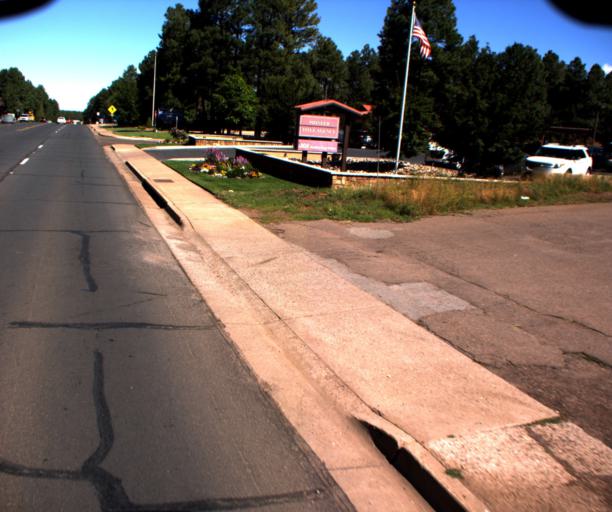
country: US
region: Arizona
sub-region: Navajo County
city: Pinetop-Lakeside
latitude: 34.1335
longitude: -109.9486
